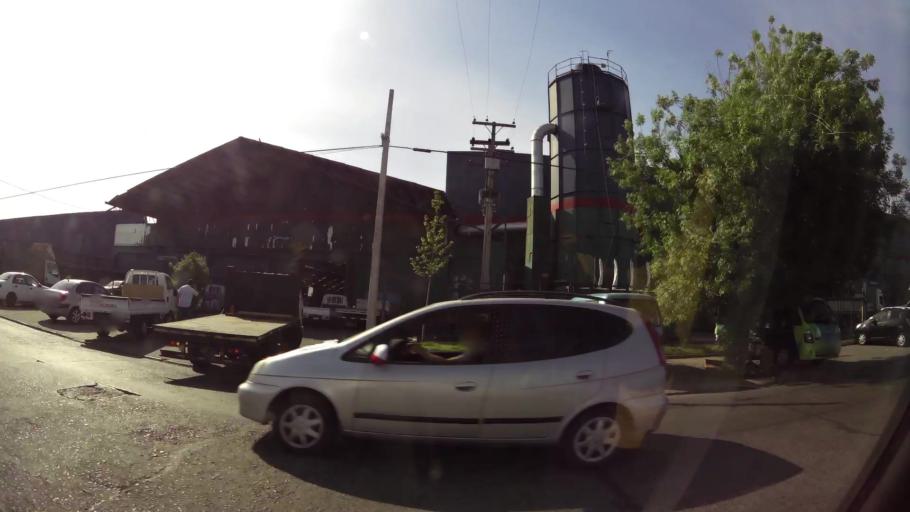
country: CL
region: Santiago Metropolitan
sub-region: Provincia de Santiago
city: La Pintana
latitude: -33.5286
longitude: -70.6327
